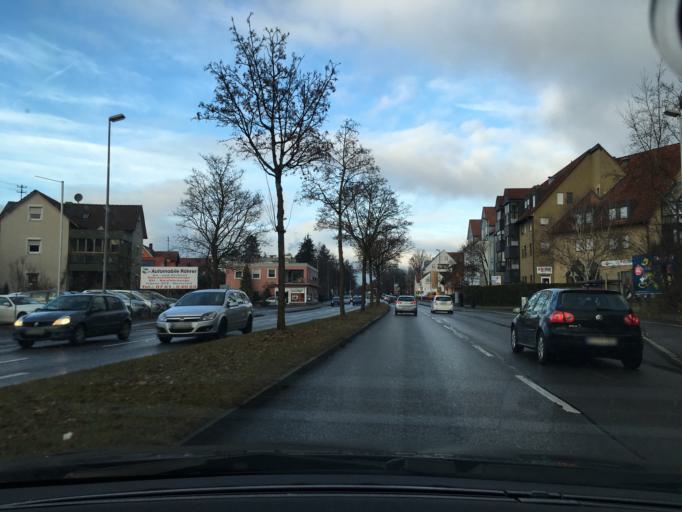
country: DE
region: Baden-Wuerttemberg
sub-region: Tuebingen Region
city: Weingarten
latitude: 47.8045
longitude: 9.6368
